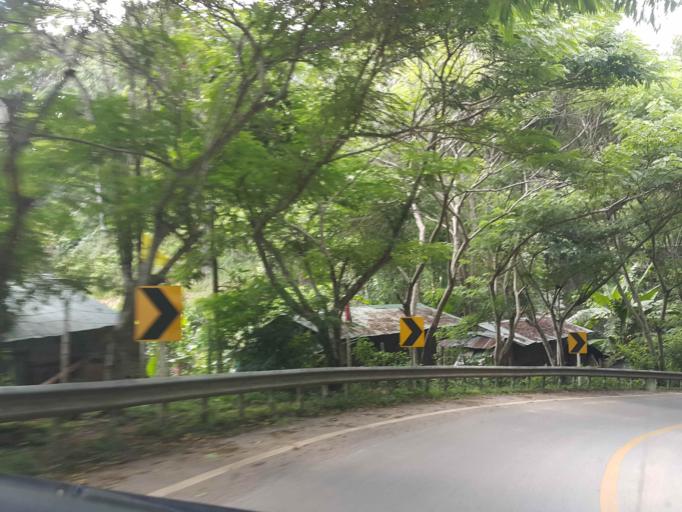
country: TH
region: Chiang Mai
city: Samoeng
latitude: 18.8762
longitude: 98.7954
